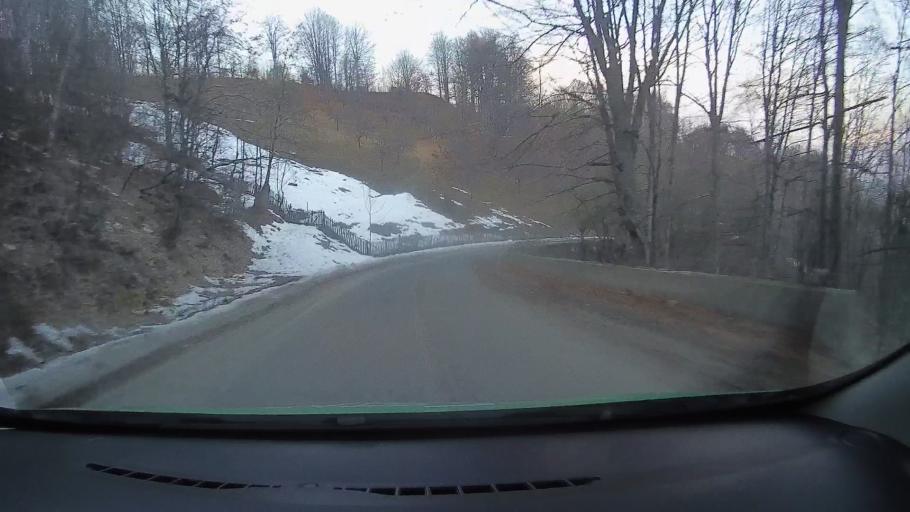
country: RO
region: Prahova
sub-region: Comuna Secaria
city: Secaria
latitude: 45.2673
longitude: 25.6751
